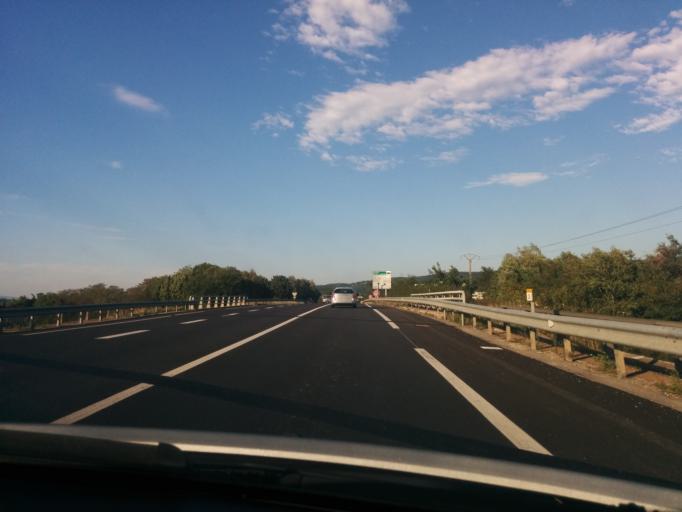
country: FR
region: Rhone-Alpes
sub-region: Departement de l'Ain
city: Amberieu-en-Bugey
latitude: 45.9746
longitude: 5.3457
